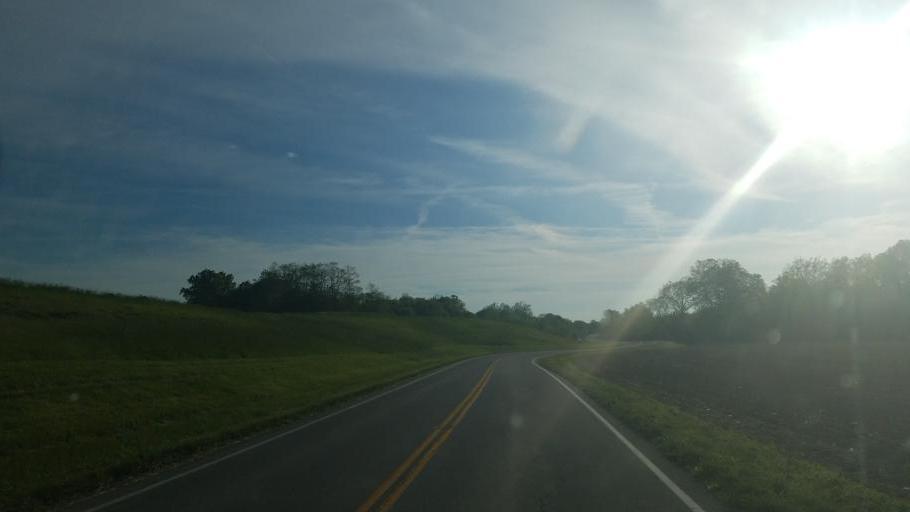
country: US
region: Ohio
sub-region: Ross County
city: Frankfort
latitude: 39.4283
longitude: -83.2287
